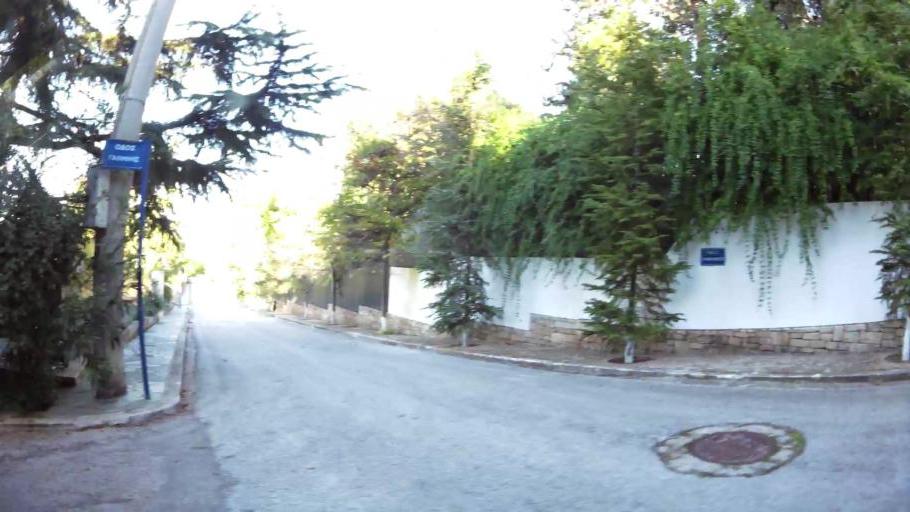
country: GR
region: Attica
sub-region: Nomarchia Athinas
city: Ekali
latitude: 38.1008
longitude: 23.8386
